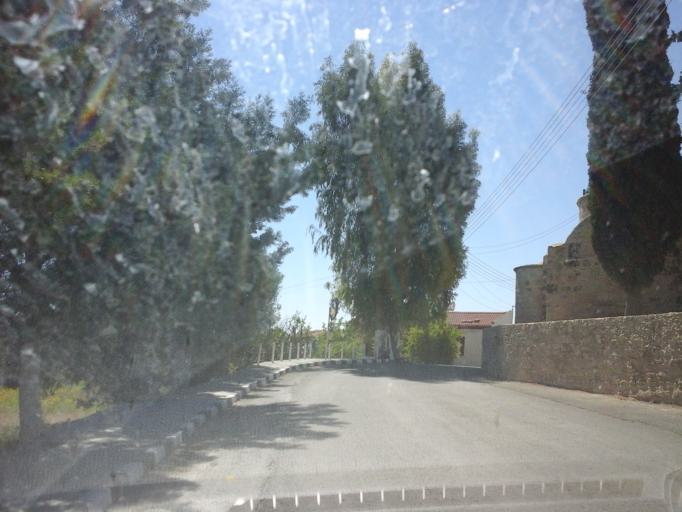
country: CY
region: Larnaka
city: Kolossi
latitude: 34.6664
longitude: 32.9344
